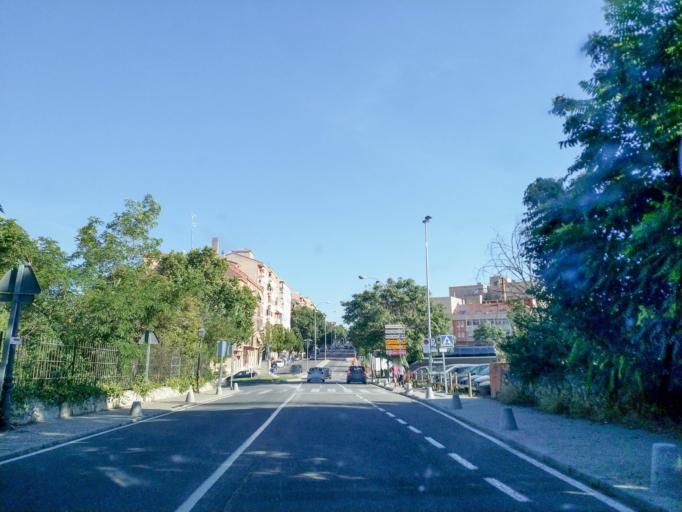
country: ES
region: Castille and Leon
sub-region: Provincia de Segovia
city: Segovia
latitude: 40.9474
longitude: -4.1246
